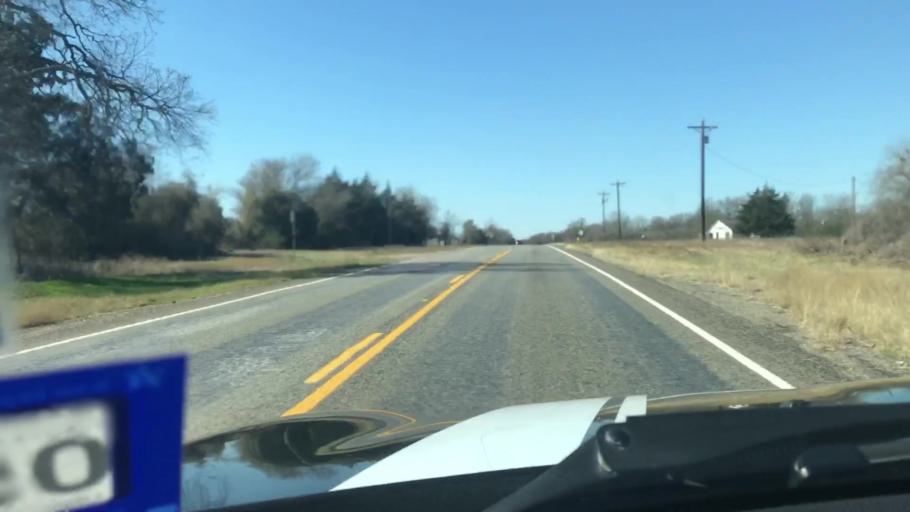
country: US
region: Texas
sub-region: Robertson County
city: Calvert
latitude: 30.8852
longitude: -96.7766
